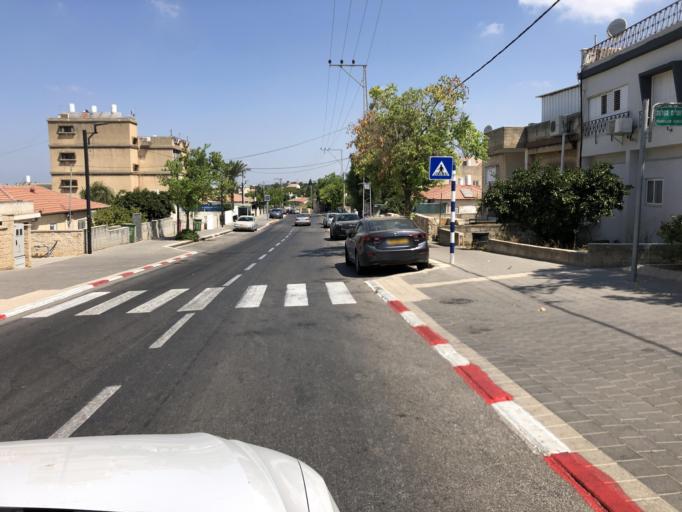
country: IL
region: Central District
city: Rosh Ha'Ayin
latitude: 32.0968
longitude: 34.9570
